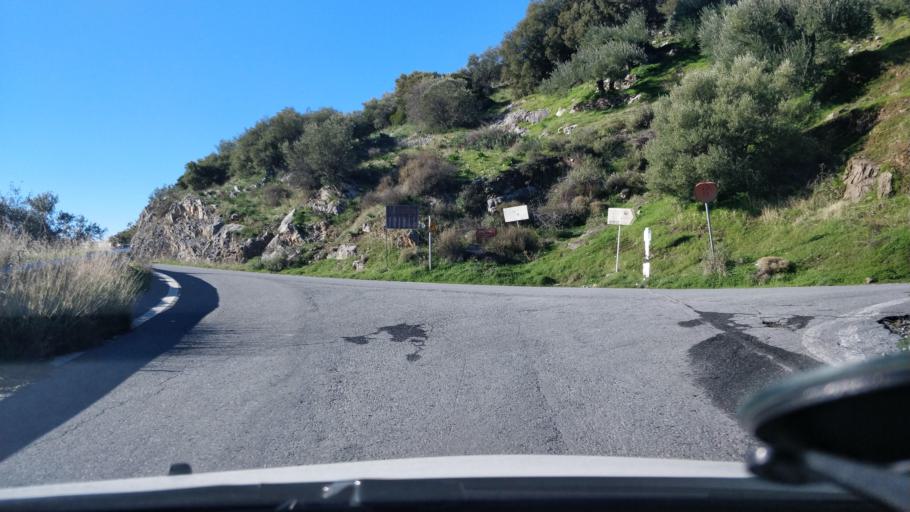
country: GR
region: Crete
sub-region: Nomos Lasithiou
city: Kritsa
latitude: 35.0792
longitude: 25.5808
